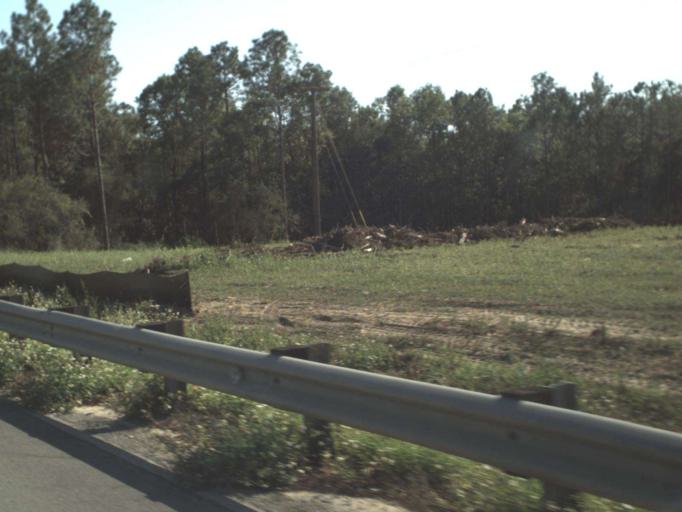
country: US
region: Florida
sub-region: Walton County
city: DeFuniak Springs
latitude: 30.6529
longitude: -86.1153
